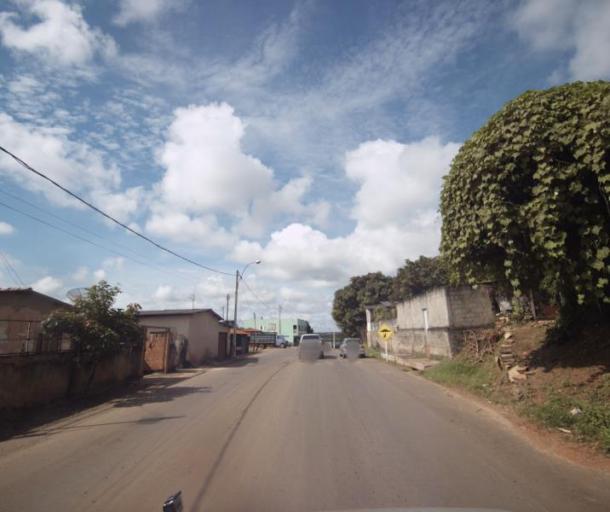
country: BR
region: Goias
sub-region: Pirenopolis
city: Pirenopolis
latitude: -15.9299
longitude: -48.8050
